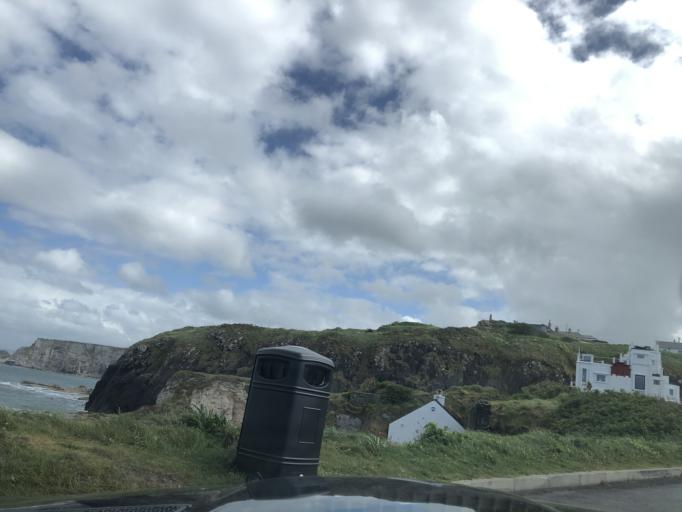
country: GB
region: Northern Ireland
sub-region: Moyle District
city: Ballycastle
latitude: 55.2447
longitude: -6.3678
